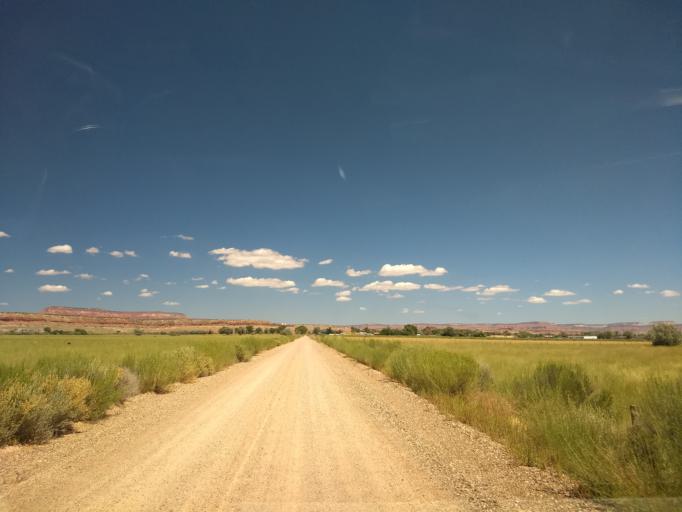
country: US
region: Arizona
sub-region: Coconino County
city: Fredonia
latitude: 36.9259
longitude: -112.5398
